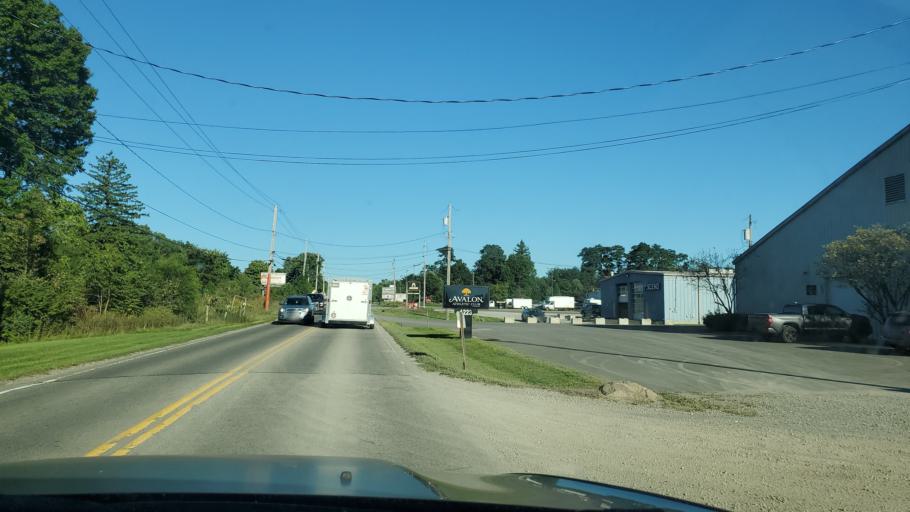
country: US
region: Ohio
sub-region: Mahoning County
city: Boardman
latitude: 40.9880
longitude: -80.6747
